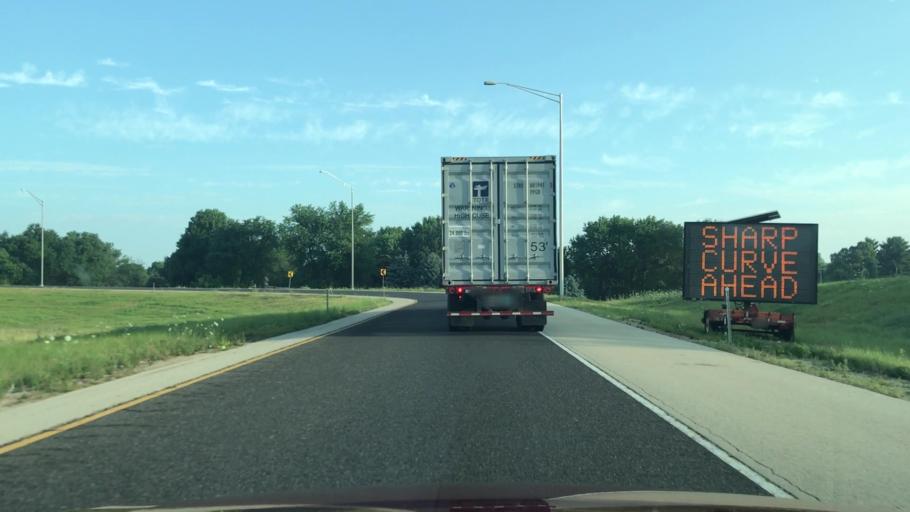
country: US
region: Illinois
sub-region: Winnebago County
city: Cherry Valley
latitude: 42.2487
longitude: -88.9584
